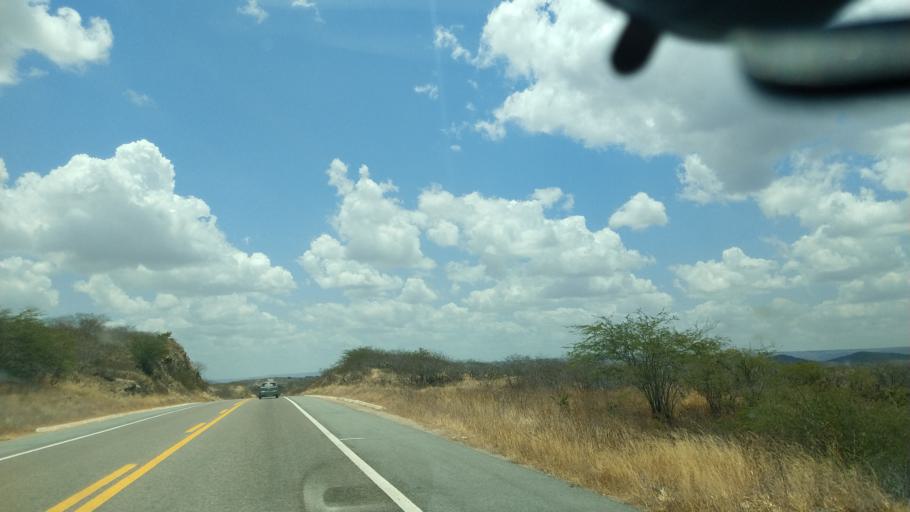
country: BR
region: Rio Grande do Norte
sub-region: Cerro Cora
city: Cerro Cora
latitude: -6.2056
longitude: -36.3221
